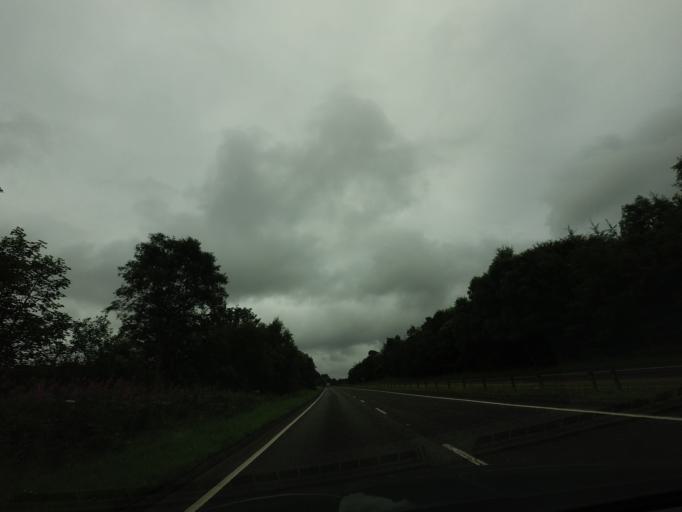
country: GB
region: Scotland
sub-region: Highland
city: Inverness
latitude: 57.4660
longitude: -4.1760
